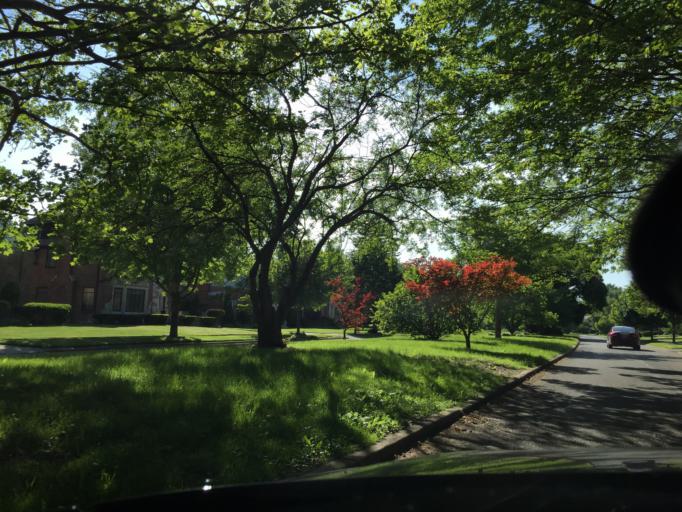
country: US
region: Michigan
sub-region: Oakland County
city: Southfield
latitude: 42.4080
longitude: -83.2286
